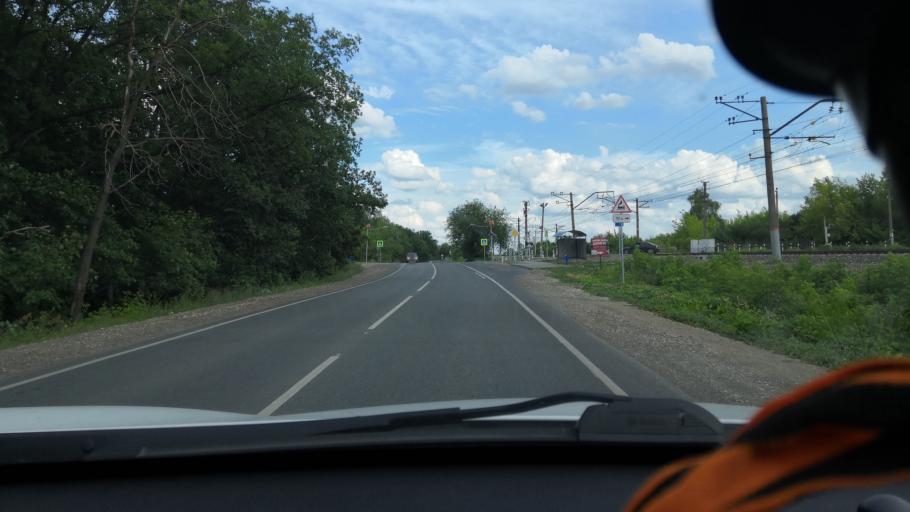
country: RU
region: Samara
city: Novosemeykino
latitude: 53.3853
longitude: 50.3288
